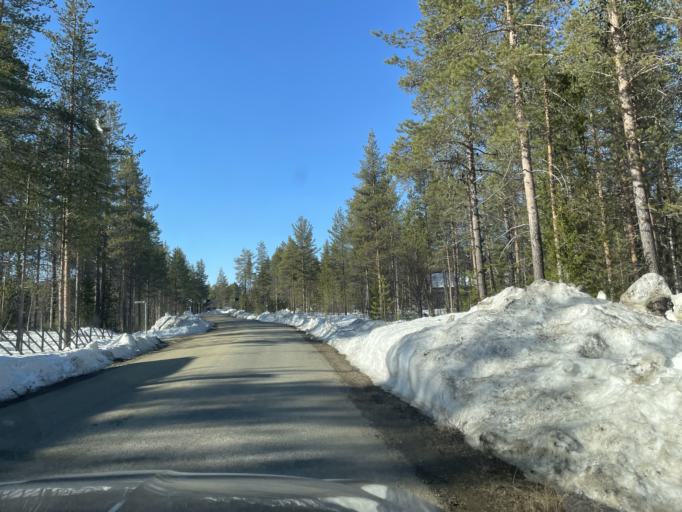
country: FI
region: Lapland
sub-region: Tunturi-Lappi
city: Kolari
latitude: 67.6082
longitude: 24.1809
